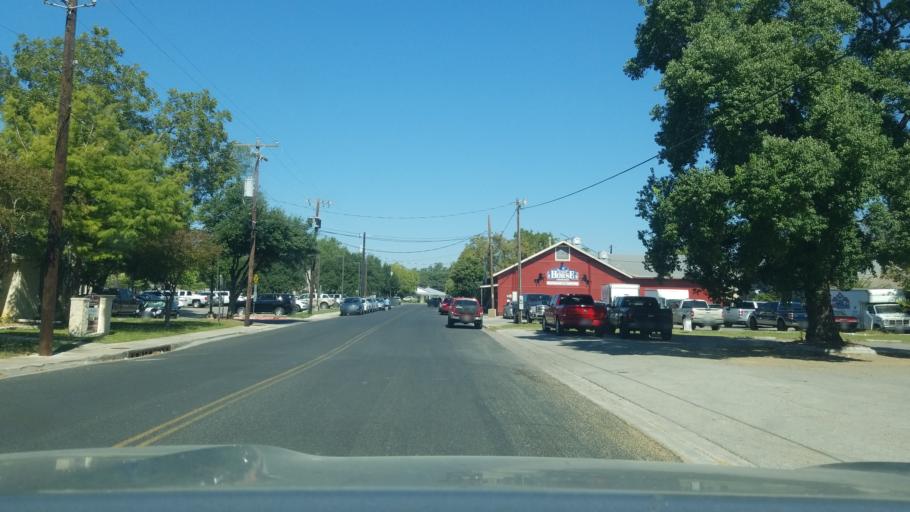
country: US
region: Texas
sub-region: Kendall County
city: Boerne
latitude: 29.7934
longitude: -98.7296
